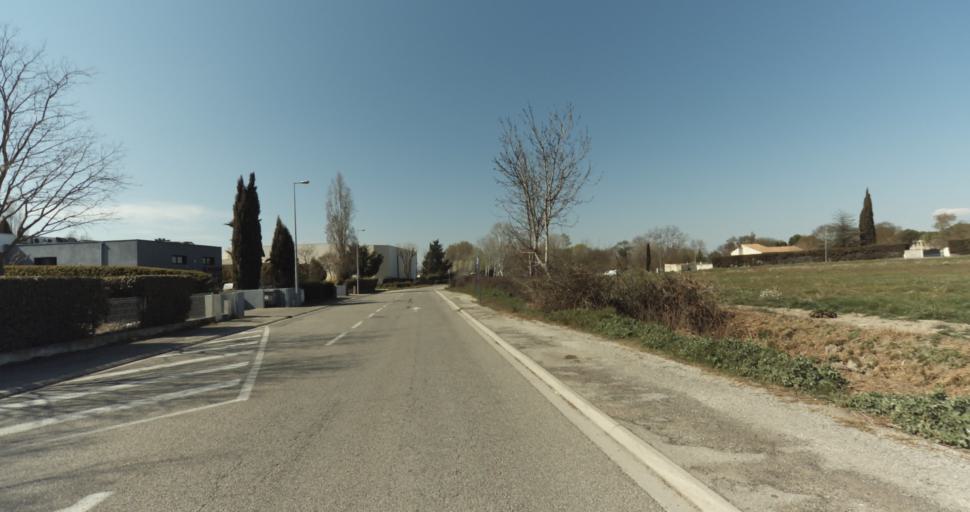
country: FR
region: Provence-Alpes-Cote d'Azur
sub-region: Departement des Bouches-du-Rhone
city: Cabries
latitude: 43.4777
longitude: 5.3791
